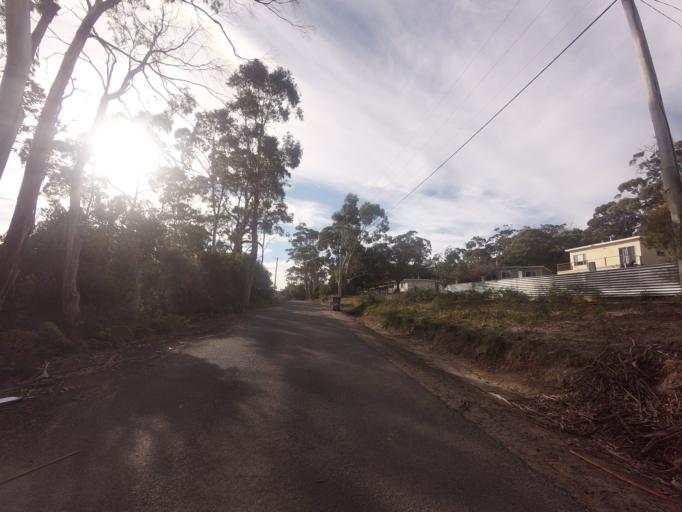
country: AU
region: Tasmania
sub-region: Sorell
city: Sorell
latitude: -42.9749
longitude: 147.8365
